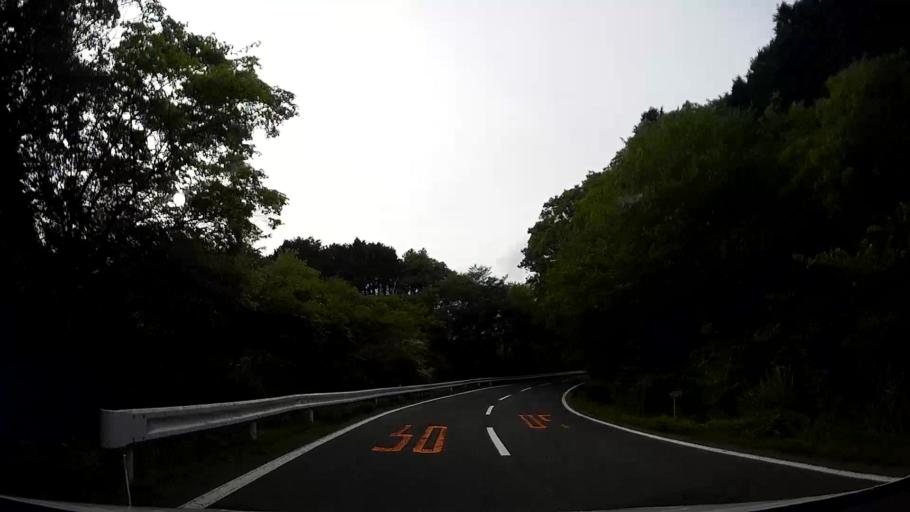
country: JP
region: Shizuoka
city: Ito
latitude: 35.0175
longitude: 139.0438
